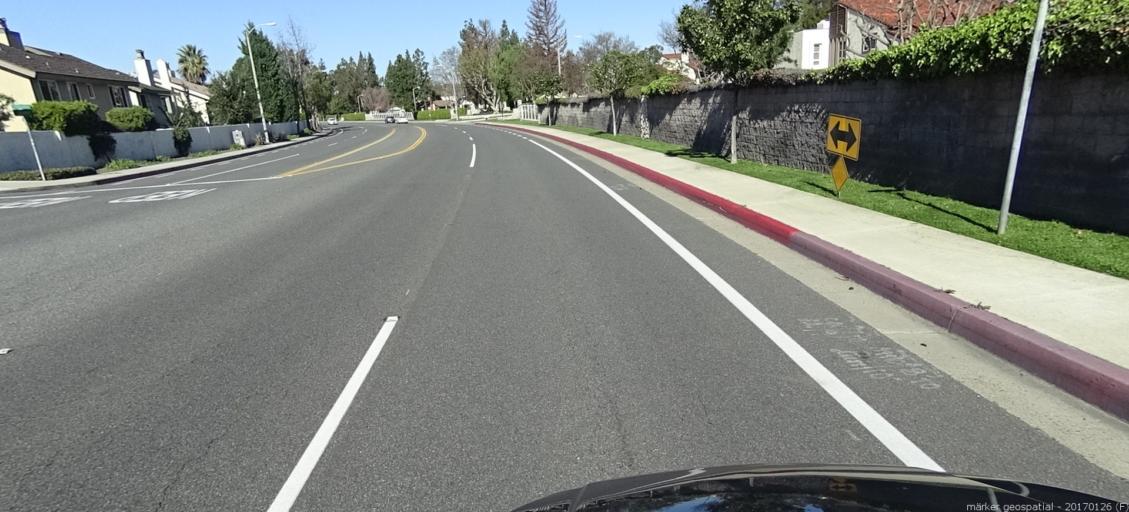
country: US
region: California
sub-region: Orange County
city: Lake Forest
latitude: 33.6417
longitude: -117.7037
